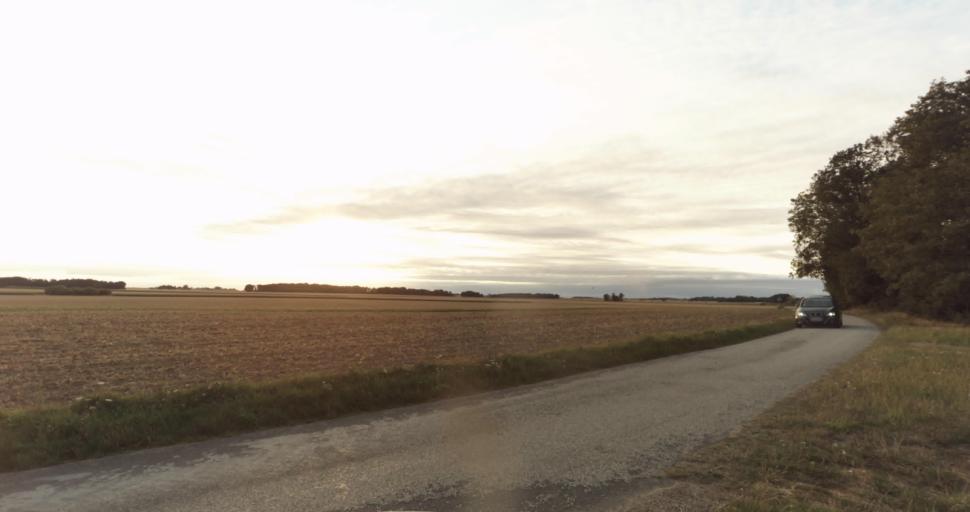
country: FR
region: Haute-Normandie
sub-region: Departement de l'Eure
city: La Madeleine-de-Nonancourt
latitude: 48.8915
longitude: 1.2367
